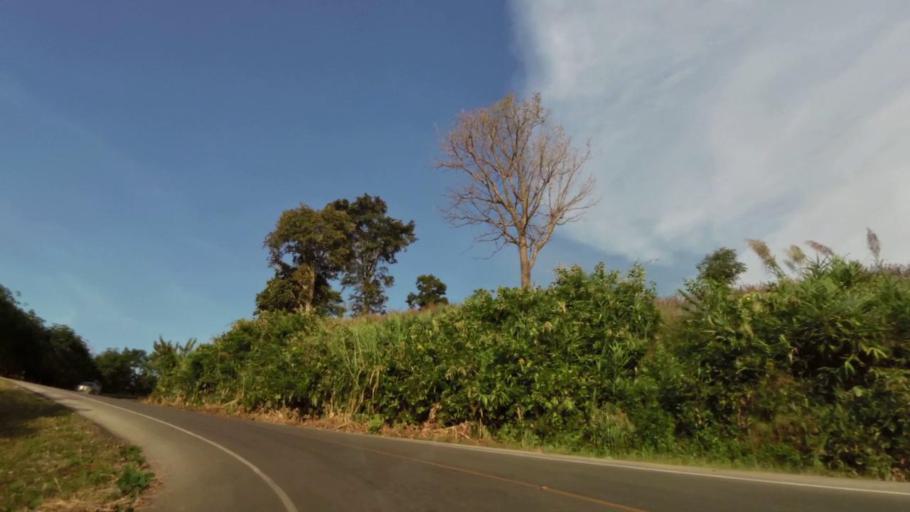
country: TH
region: Chiang Rai
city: Khun Tan
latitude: 19.8635
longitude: 100.4183
